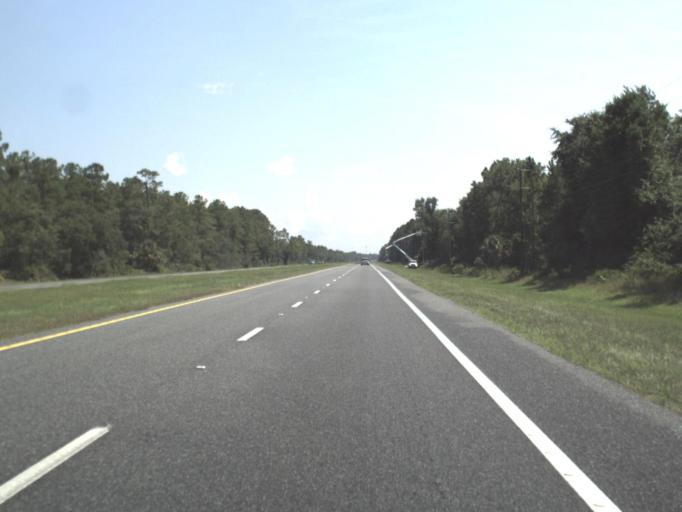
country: US
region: Florida
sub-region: Levy County
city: Inglis
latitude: 29.1459
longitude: -82.6381
